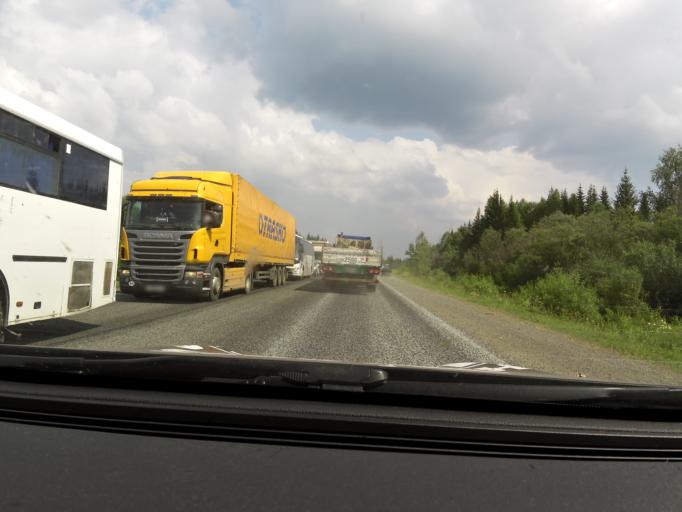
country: RU
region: Sverdlovsk
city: Ufimskiy
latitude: 56.7713
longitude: 58.1132
